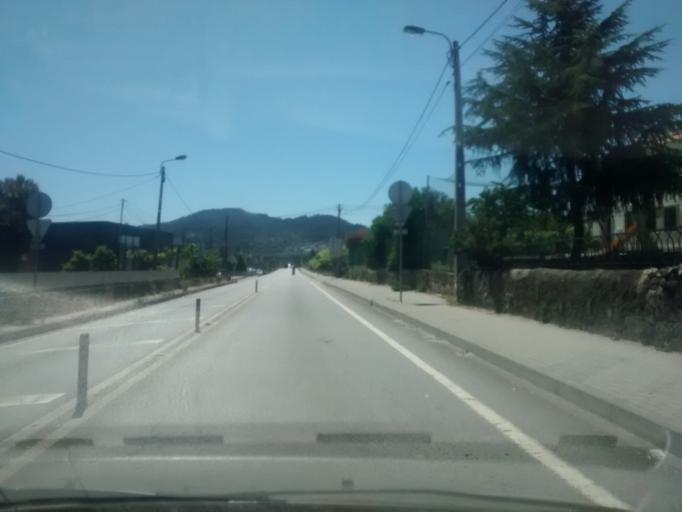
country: PT
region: Braga
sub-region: Braga
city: Oliveira
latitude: 41.5320
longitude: -8.4727
